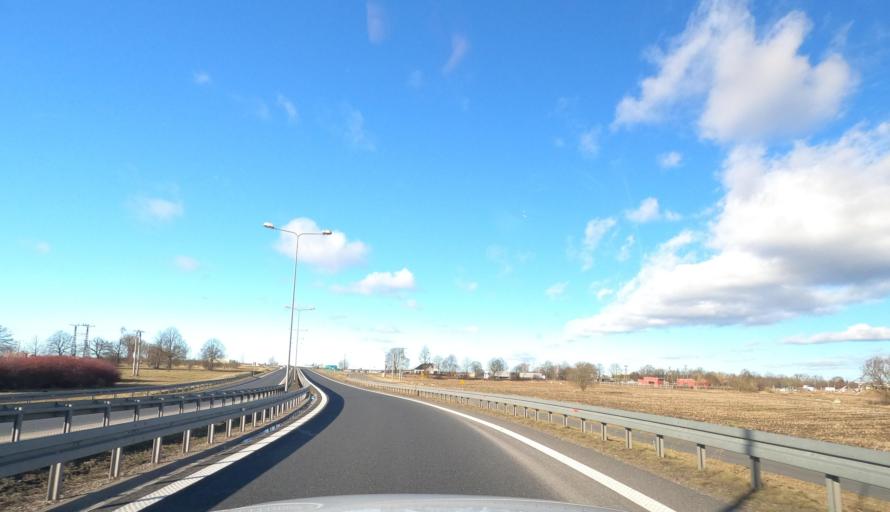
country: PL
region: West Pomeranian Voivodeship
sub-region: Powiat stargardzki
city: Stargard Szczecinski
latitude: 53.3075
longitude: 15.0277
